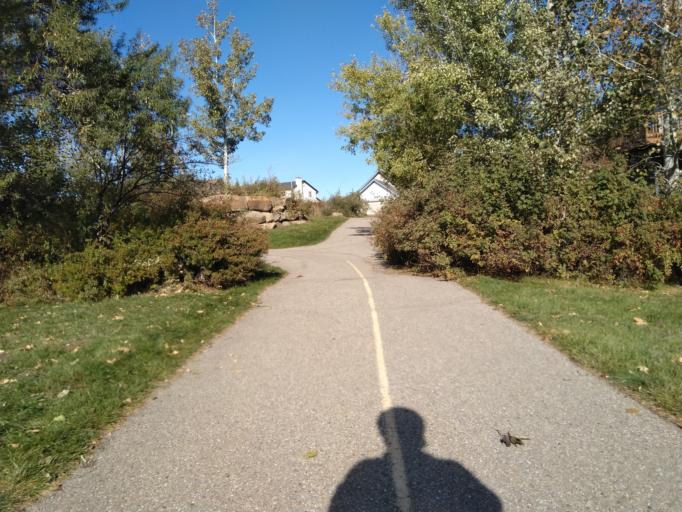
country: CA
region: Alberta
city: Calgary
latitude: 51.1634
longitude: -114.1208
